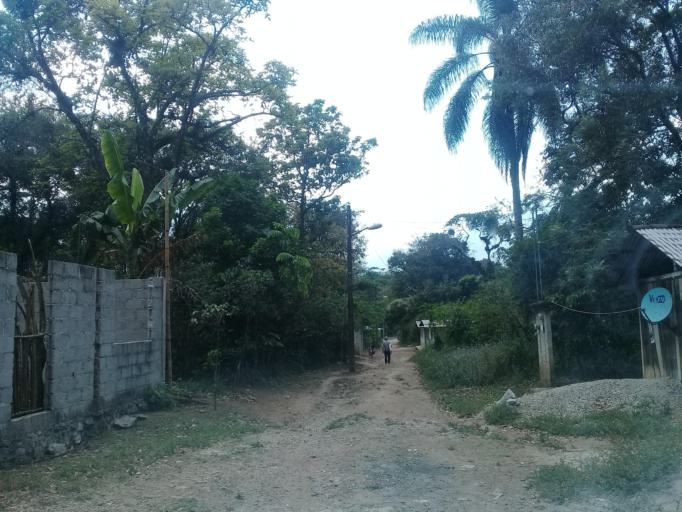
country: MX
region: Veracruz
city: Jalapilla
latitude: 18.8202
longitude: -97.0618
